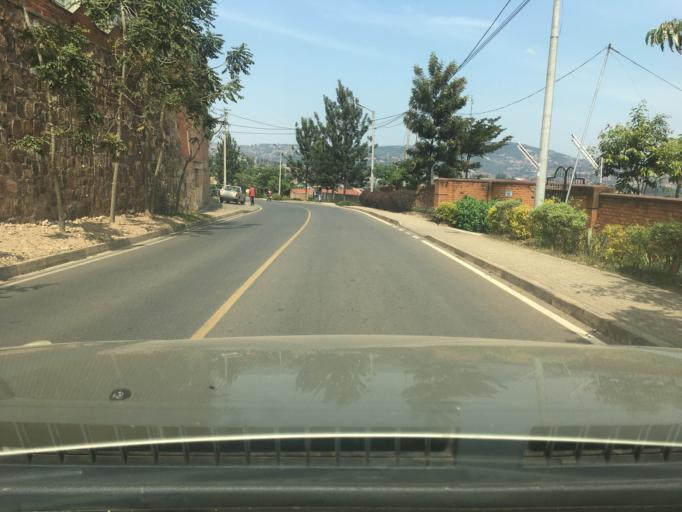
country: RW
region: Kigali
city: Kigali
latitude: -1.9578
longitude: 30.1030
